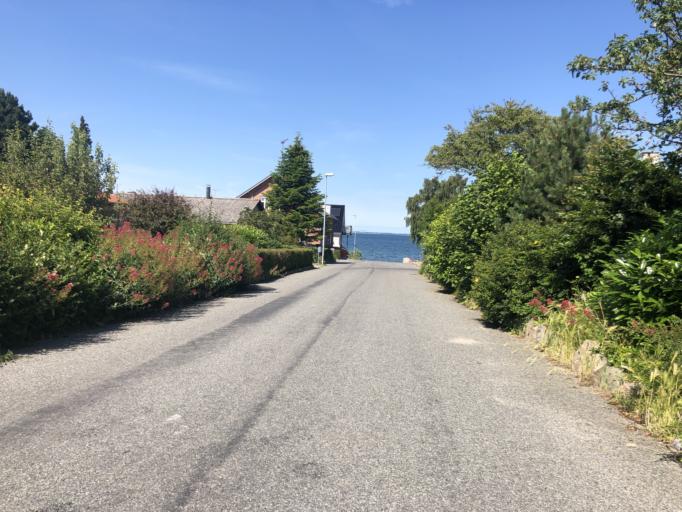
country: DK
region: South Denmark
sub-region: AEro Kommune
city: Marstal
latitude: 54.8602
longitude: 10.5164
